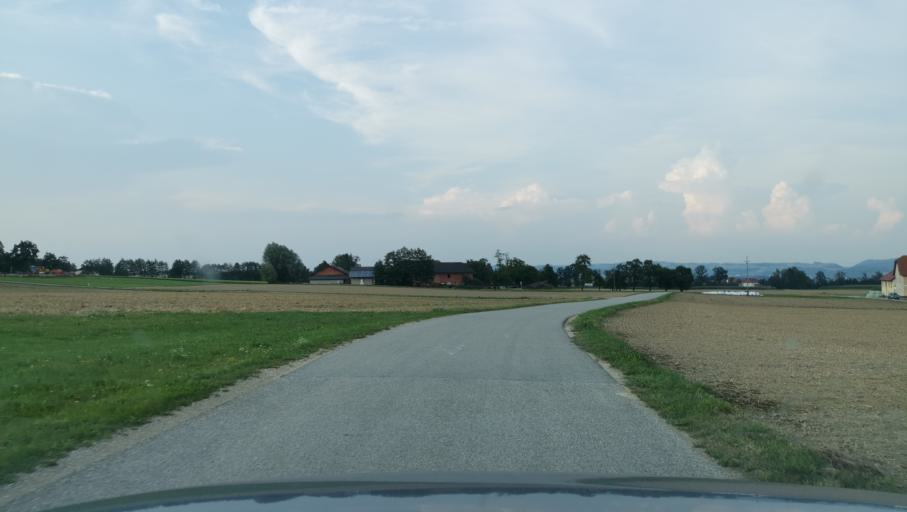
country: AT
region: Upper Austria
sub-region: Politischer Bezirk Grieskirchen
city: Grieskirchen
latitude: 48.3042
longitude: 13.8113
